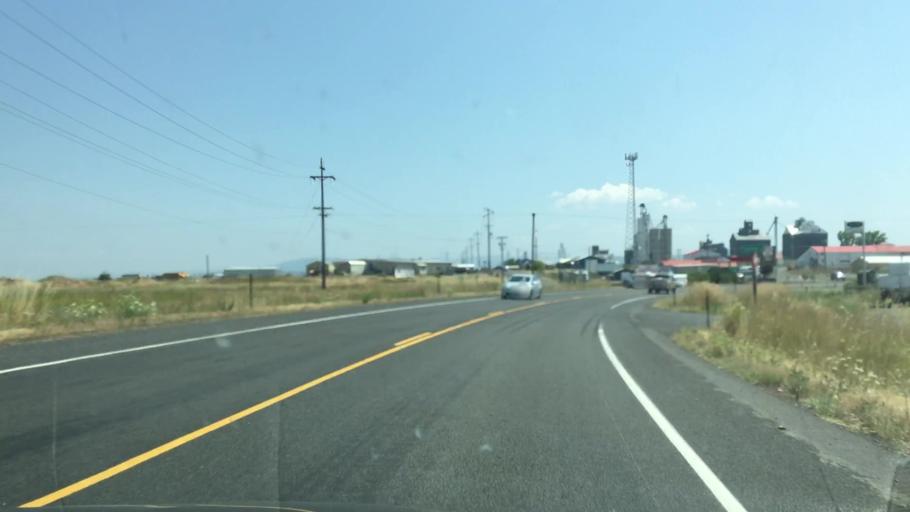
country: US
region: Idaho
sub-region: Idaho County
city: Grangeville
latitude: 45.9360
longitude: -116.1363
